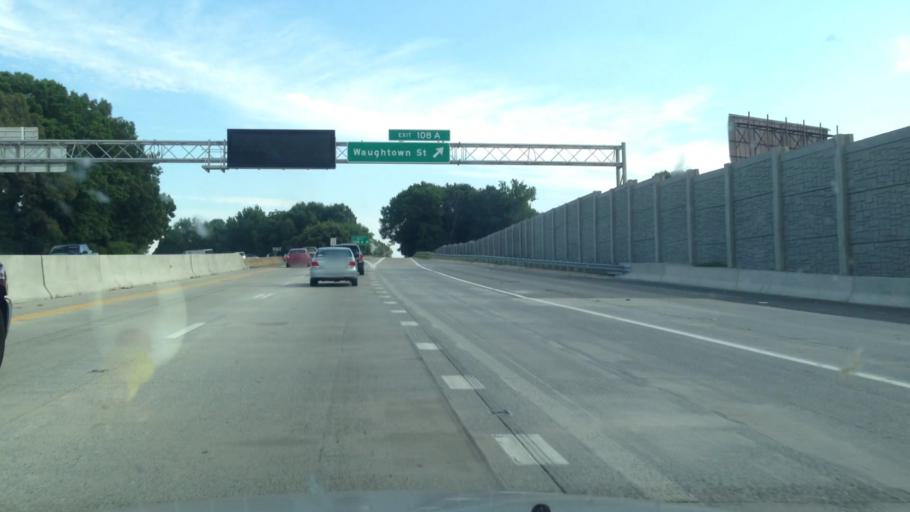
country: US
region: North Carolina
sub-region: Forsyth County
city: Winston-Salem
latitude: 36.0771
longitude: -80.2307
